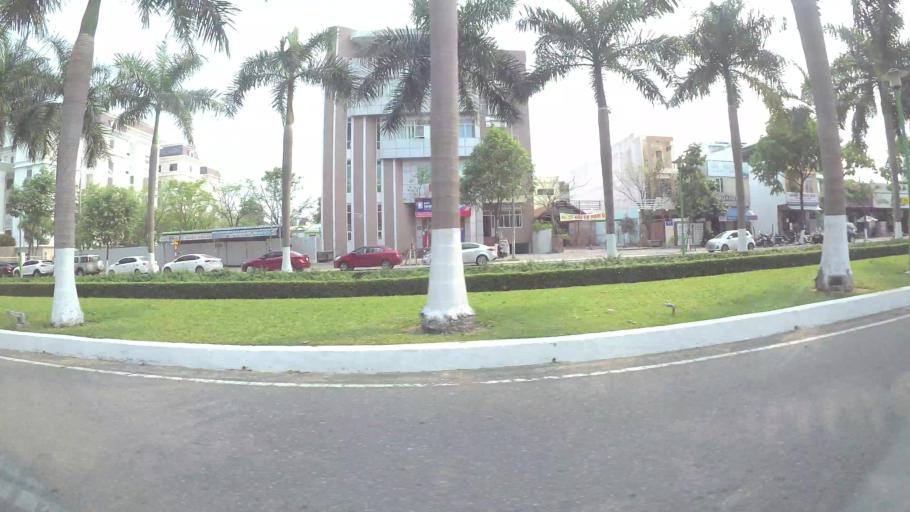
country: VN
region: Da Nang
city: Son Tra
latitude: 16.0407
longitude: 108.2205
